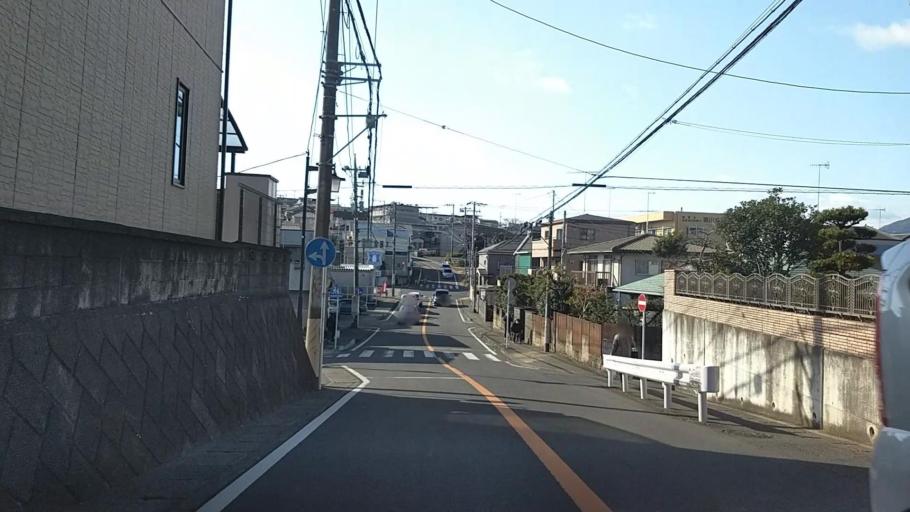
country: JP
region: Kanagawa
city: Isehara
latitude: 35.3930
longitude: 139.3116
